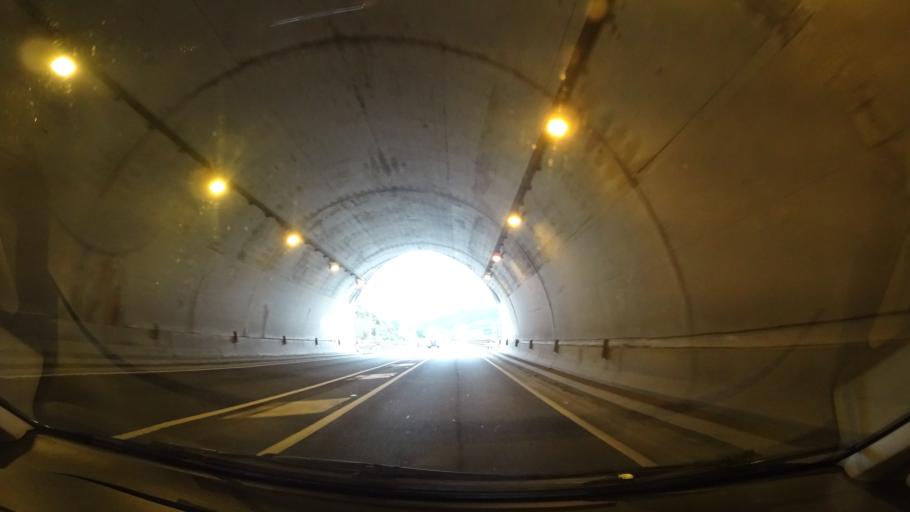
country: ES
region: Basque Country
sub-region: Bizkaia
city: Areatza
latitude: 43.1734
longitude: -2.7732
